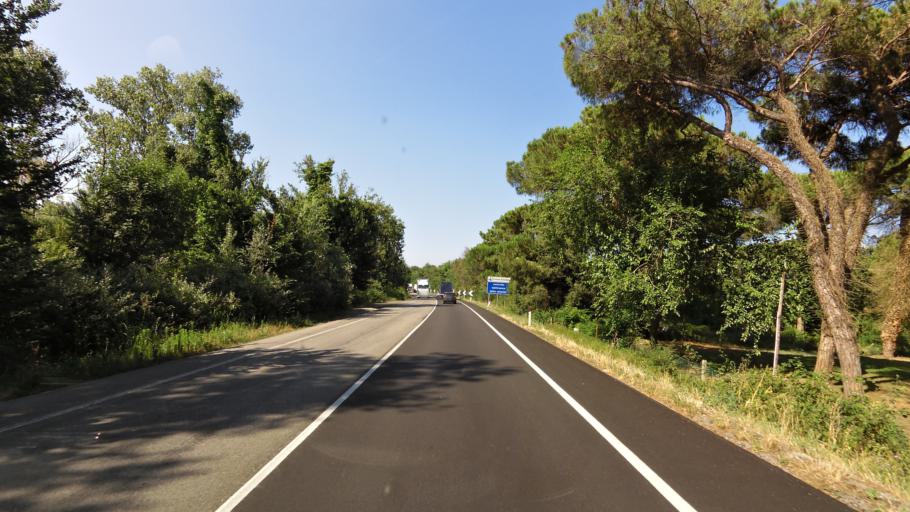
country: IT
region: Emilia-Romagna
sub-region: Provincia di Ravenna
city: Marina Romea
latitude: 44.5137
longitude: 12.2260
